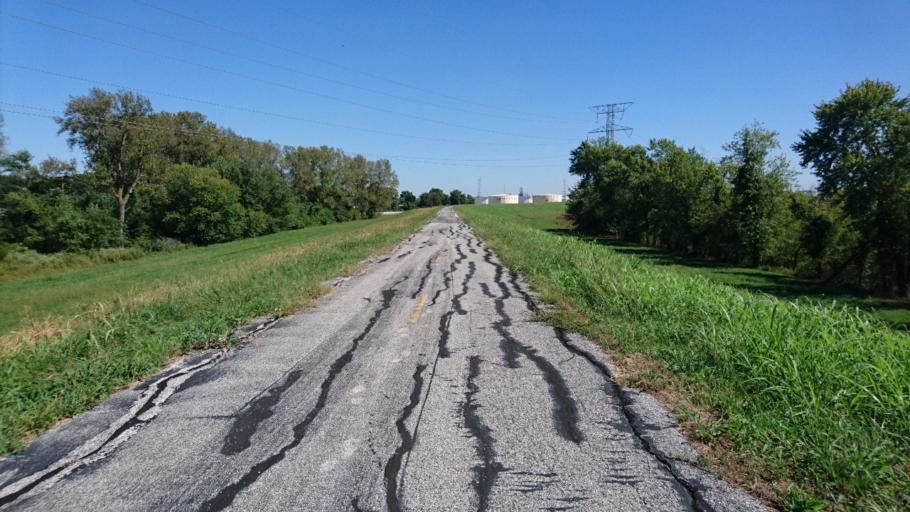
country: US
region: Illinois
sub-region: Madison County
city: Wood River
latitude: 38.8552
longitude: -90.1091
